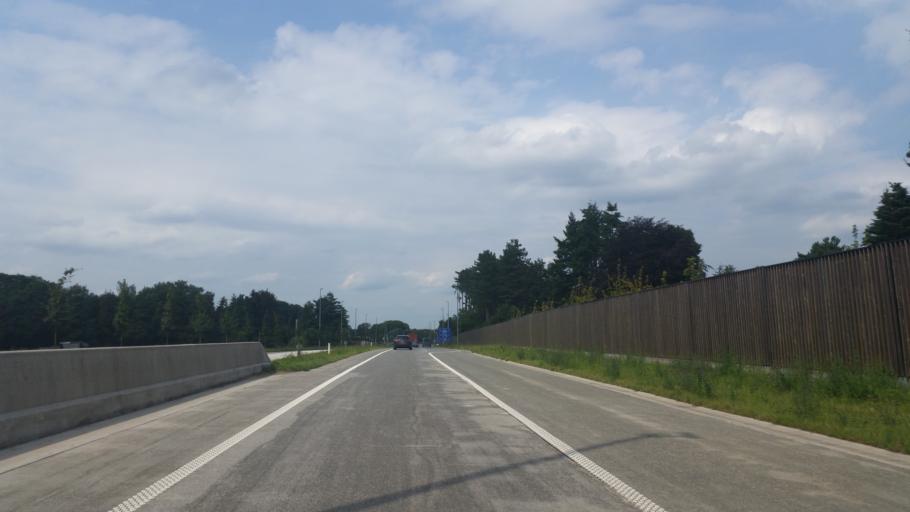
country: BE
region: Flanders
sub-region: Provincie Antwerpen
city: Kasterlee
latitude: 51.2351
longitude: 4.9582
